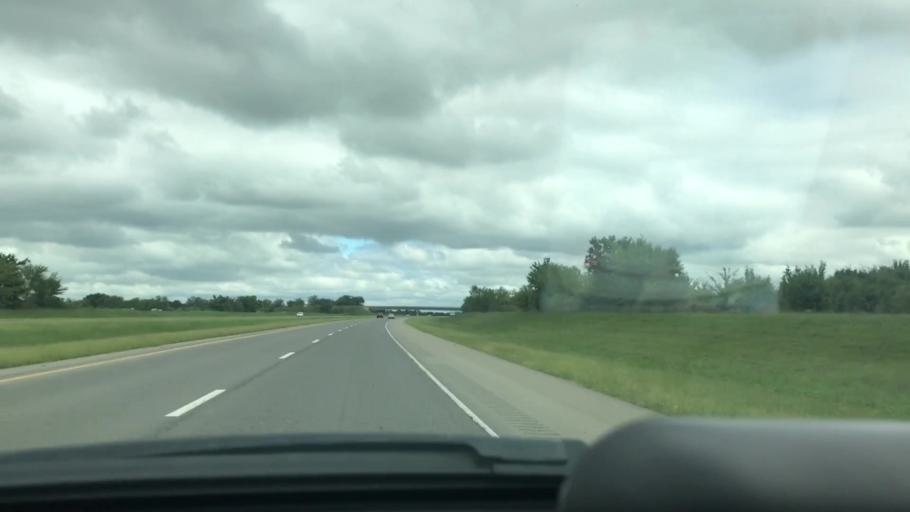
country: US
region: Oklahoma
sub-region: McIntosh County
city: Checotah
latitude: 35.5898
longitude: -95.4879
